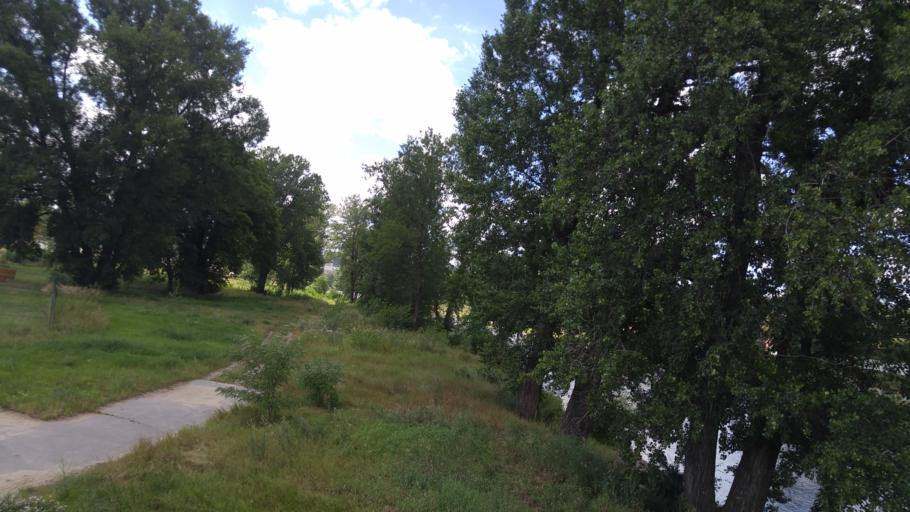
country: CZ
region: Praha
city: Prague
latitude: 50.1138
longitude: 14.4167
